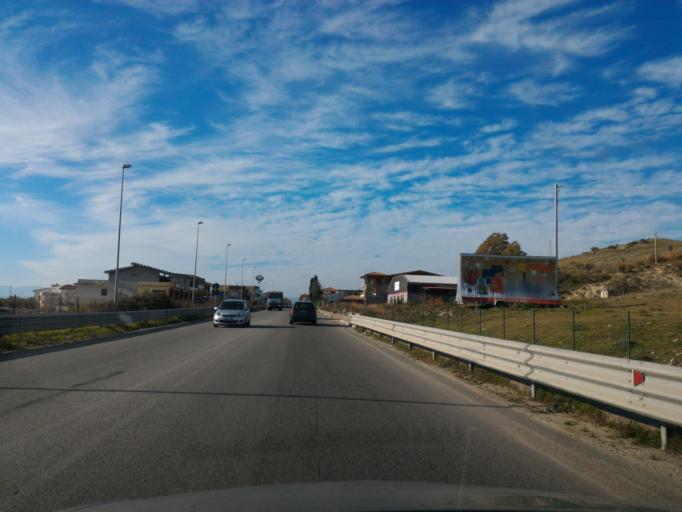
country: IT
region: Calabria
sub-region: Provincia di Catanzaro
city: Cropani Marina
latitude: 38.9217
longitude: 16.8030
